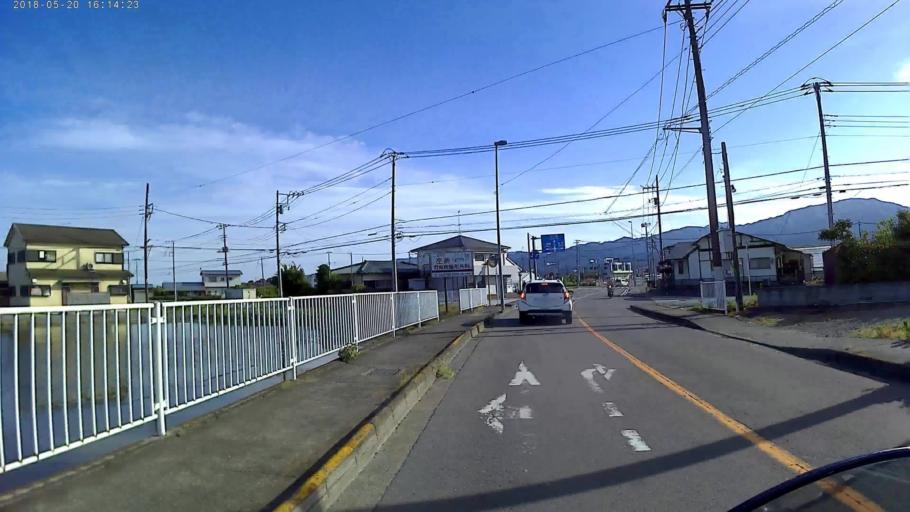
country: JP
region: Kanagawa
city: Odawara
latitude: 35.3147
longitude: 139.1541
